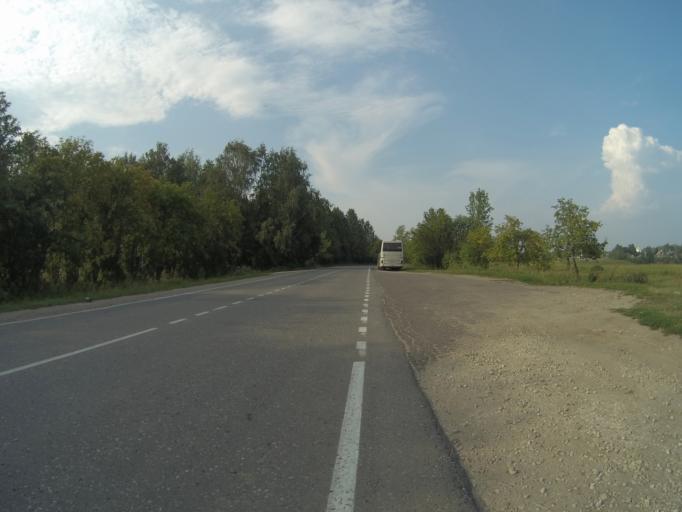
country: RU
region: Vladimir
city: Suzdal'
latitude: 56.4190
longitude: 40.4281
